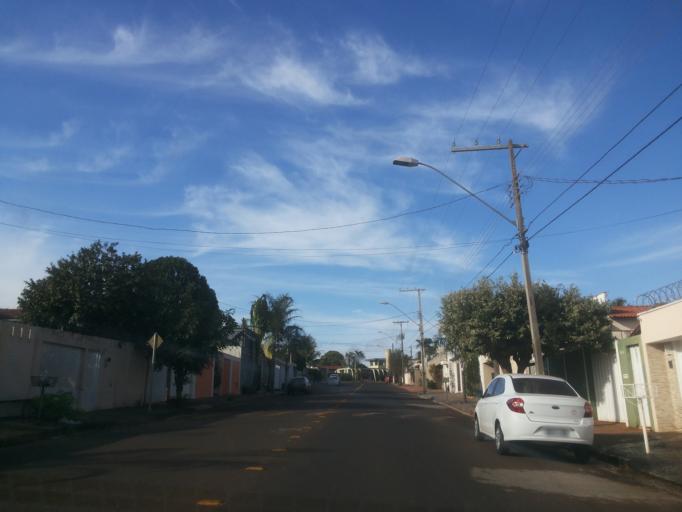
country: BR
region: Minas Gerais
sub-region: Ituiutaba
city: Ituiutaba
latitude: -18.9869
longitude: -49.4609
